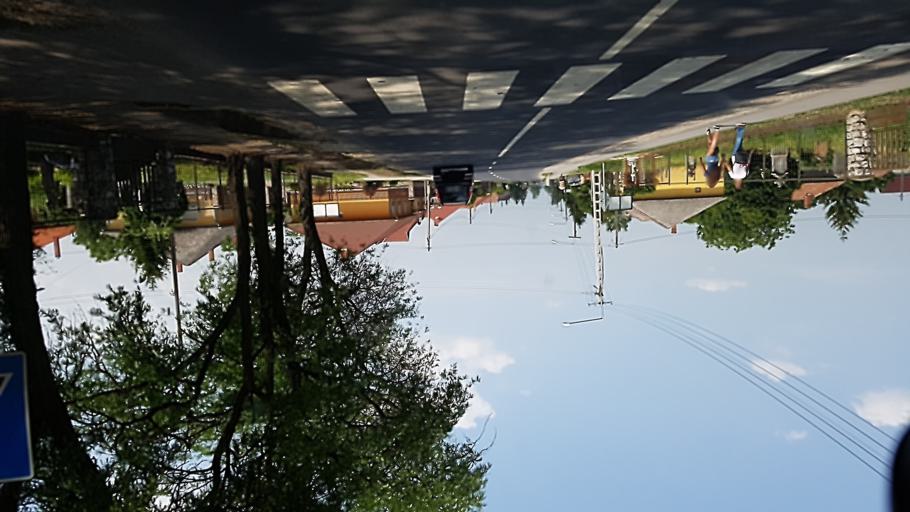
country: HU
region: Heves
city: Besenyotelek
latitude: 47.6947
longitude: 20.4350
